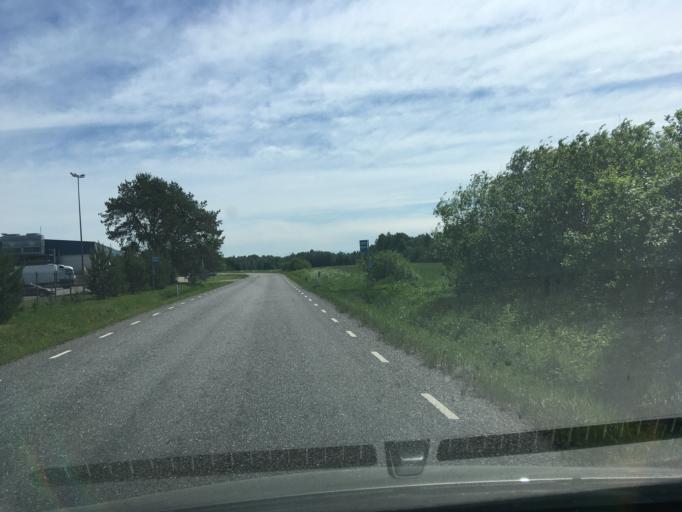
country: EE
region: Paernumaa
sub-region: Audru vald
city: Audru
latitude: 58.4264
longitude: 24.4254
